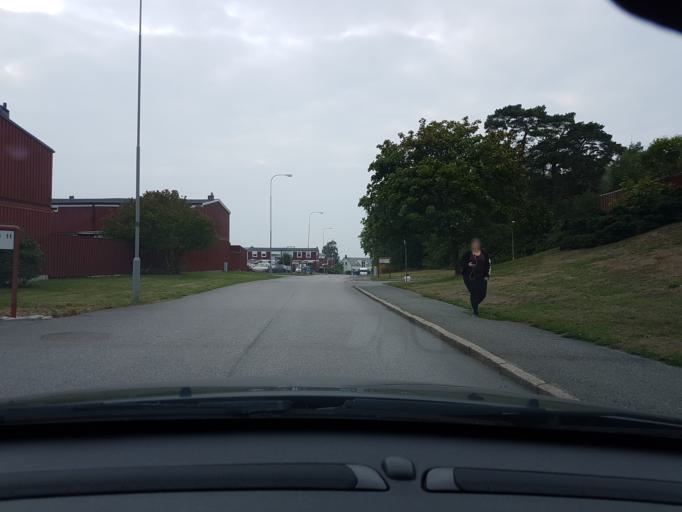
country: SE
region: Vaestra Goetaland
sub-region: Goteborg
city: Majorna
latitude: 57.6411
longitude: 11.8916
